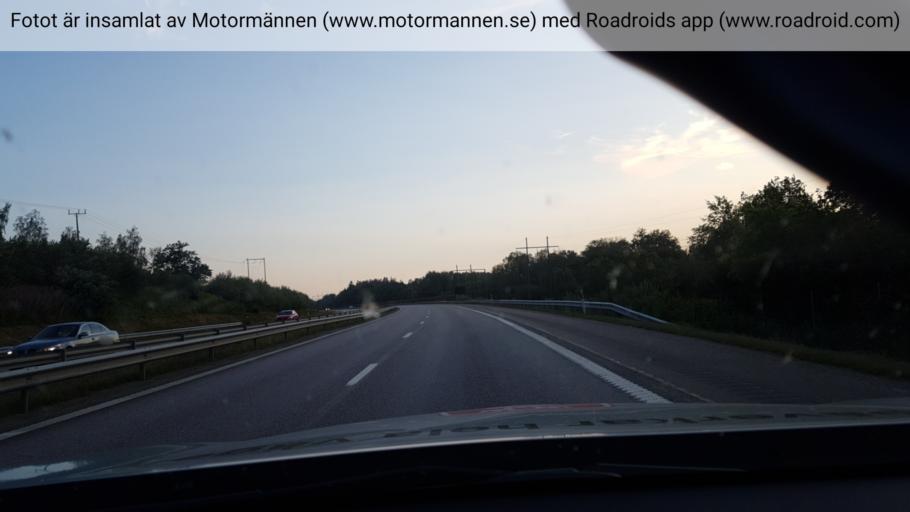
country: SE
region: Vaestra Goetaland
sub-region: Boras Kommun
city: Sjomarken
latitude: 57.7099
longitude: 12.8514
